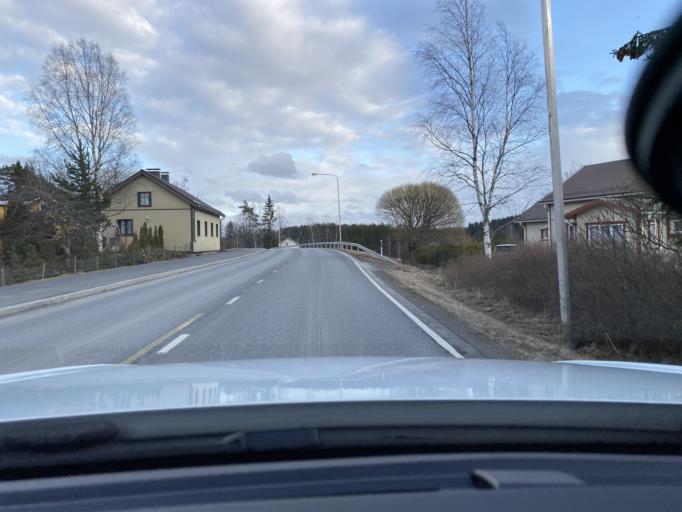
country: FI
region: Pirkanmaa
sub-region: Lounais-Pirkanmaa
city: Punkalaidun
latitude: 61.1193
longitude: 23.0720
